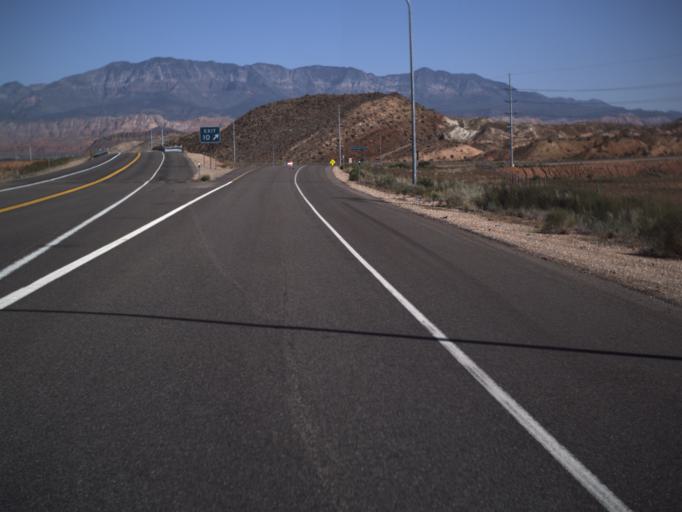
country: US
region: Utah
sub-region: Washington County
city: Washington
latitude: 37.0561
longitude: -113.4857
